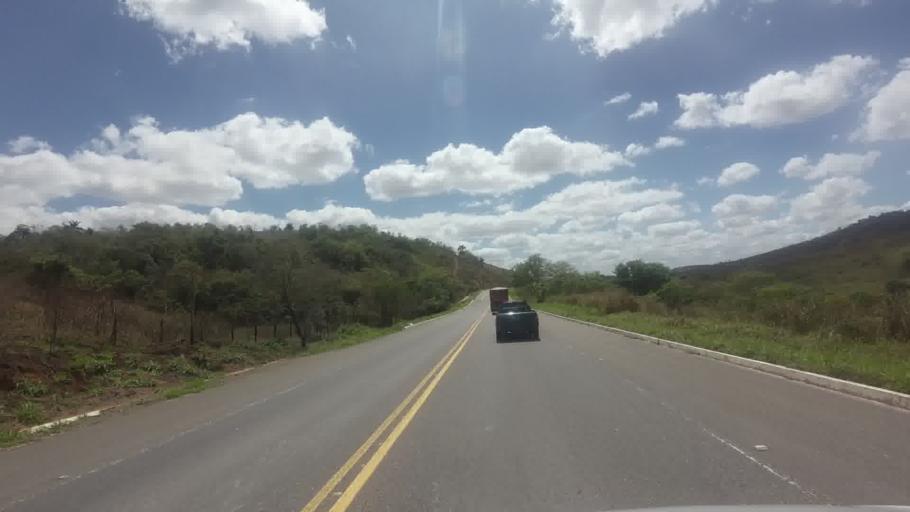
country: BR
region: Minas Gerais
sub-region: Recreio
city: Recreio
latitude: -21.6705
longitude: -42.3903
